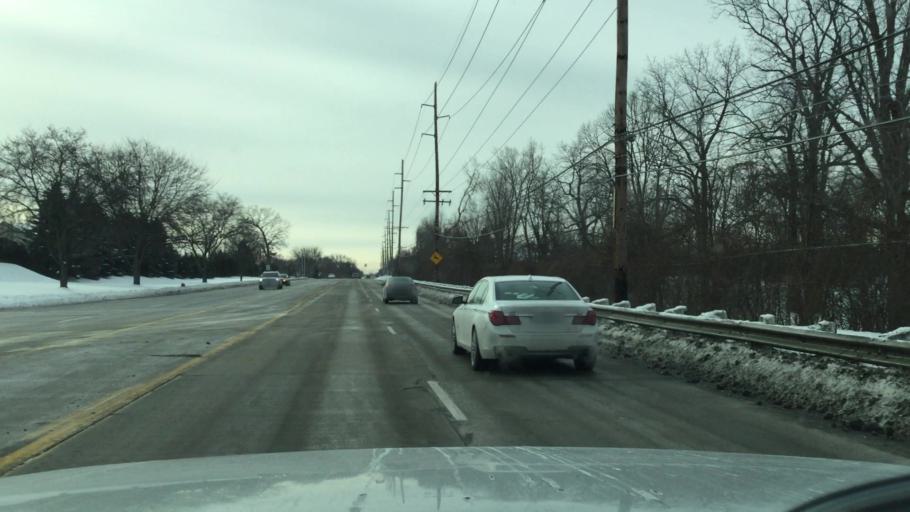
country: US
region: Michigan
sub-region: Oakland County
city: Troy
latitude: 42.6051
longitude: -83.1298
